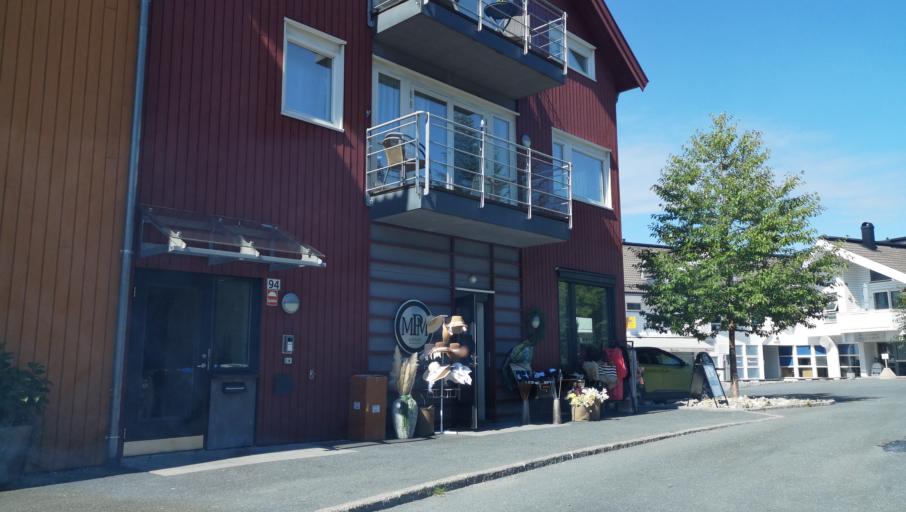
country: NO
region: Ostfold
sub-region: Moss
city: Moss
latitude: 59.5251
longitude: 10.6882
